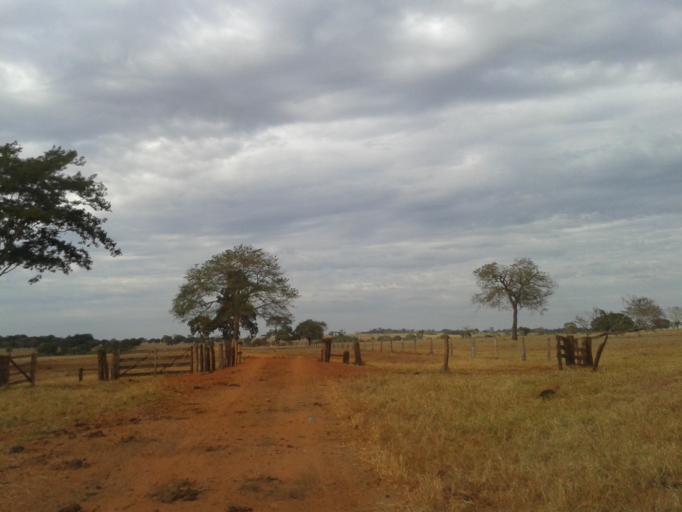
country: BR
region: Minas Gerais
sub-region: Santa Vitoria
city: Santa Vitoria
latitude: -18.7576
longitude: -50.1945
